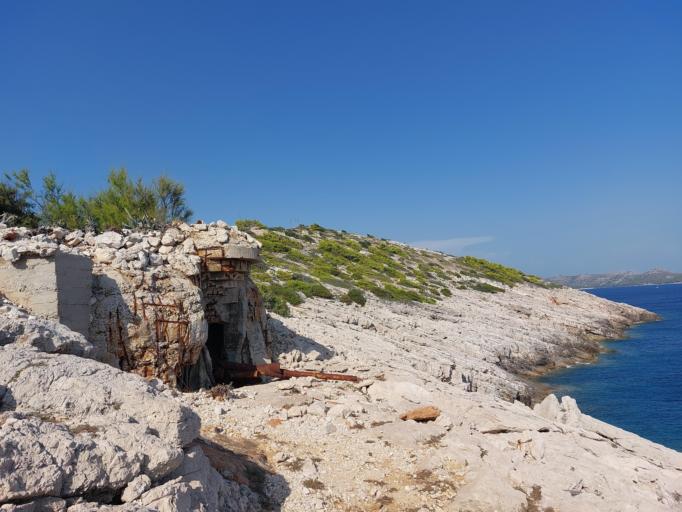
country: HR
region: Dubrovacko-Neretvanska
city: Smokvica
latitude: 42.7233
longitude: 16.8423
